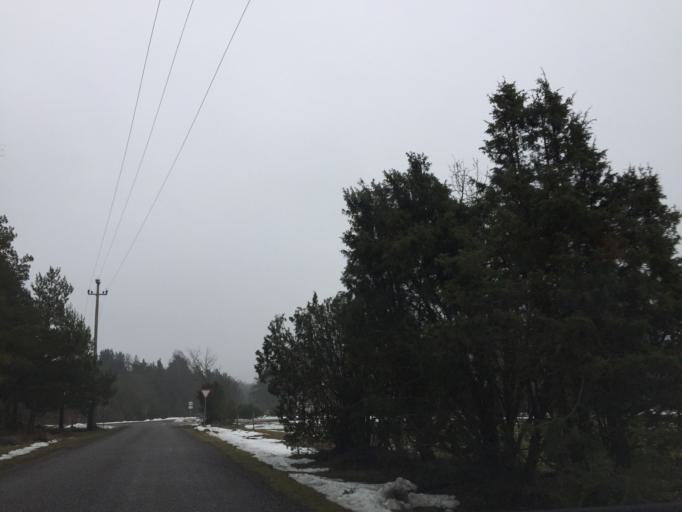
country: EE
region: Saare
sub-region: Kuressaare linn
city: Kuressaare
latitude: 58.2702
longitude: 22.5848
